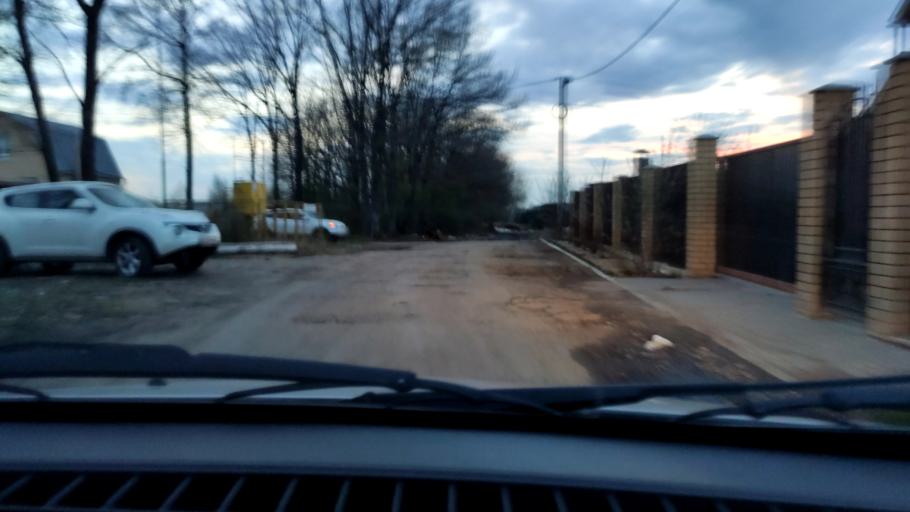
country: RU
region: Voronezj
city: Podgornoye
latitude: 51.7976
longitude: 39.2156
